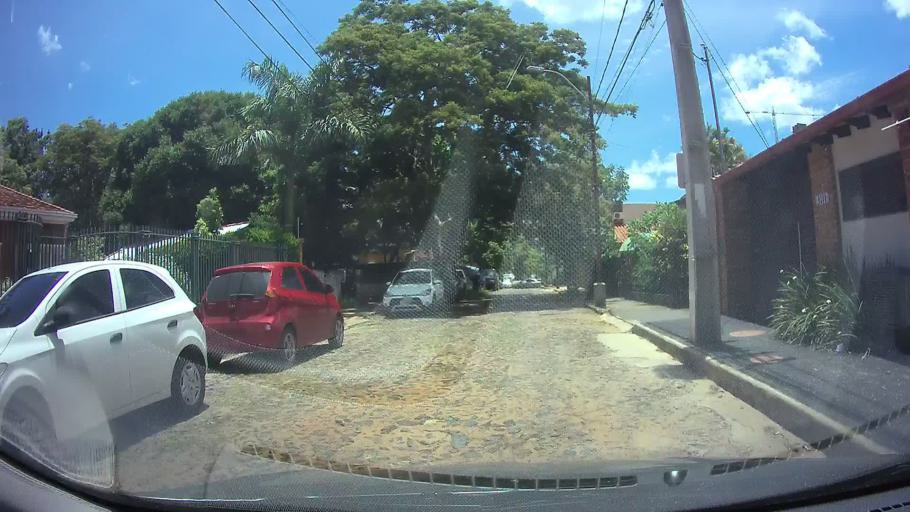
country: PY
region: Central
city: Fernando de la Mora
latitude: -25.3018
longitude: -57.5679
